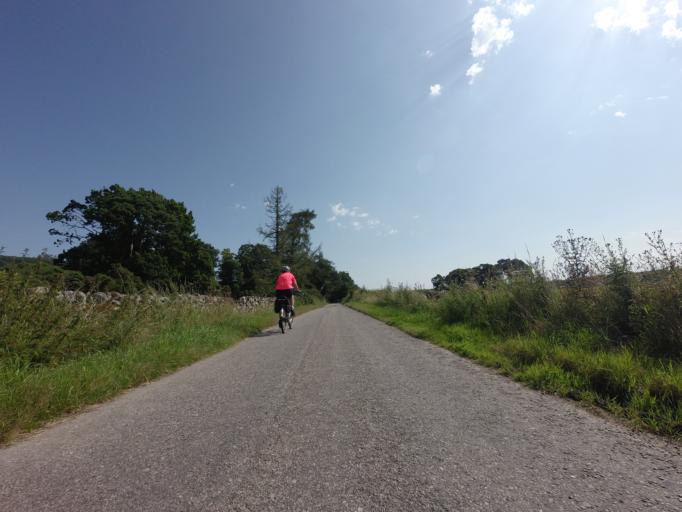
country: GB
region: Scotland
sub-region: Highland
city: Invergordon
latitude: 57.7548
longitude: -4.1486
